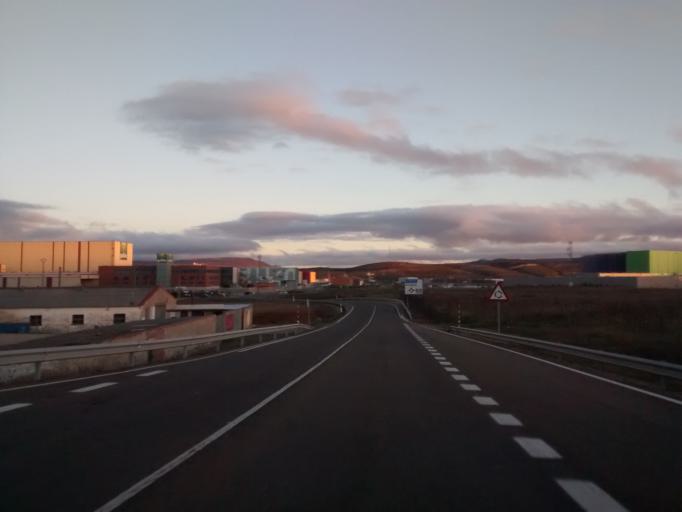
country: ES
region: Castille and Leon
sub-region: Provincia de Palencia
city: Aguilar de Campoo
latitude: 42.7903
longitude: -4.2473
